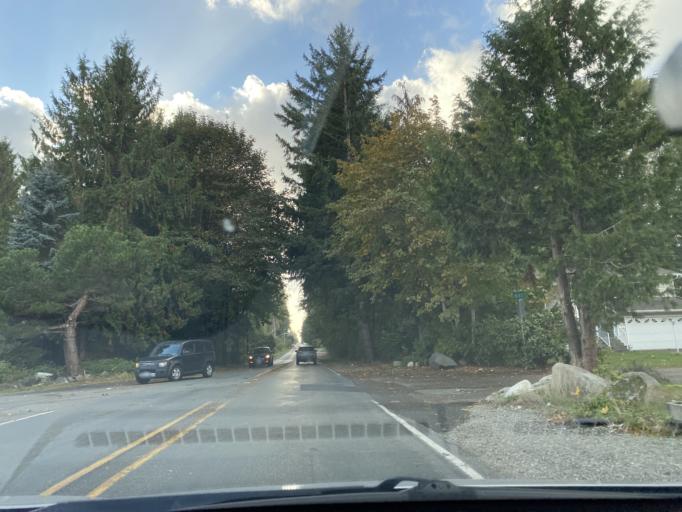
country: US
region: Washington
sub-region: Pierce County
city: South Hill
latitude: 47.1184
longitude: -122.2710
